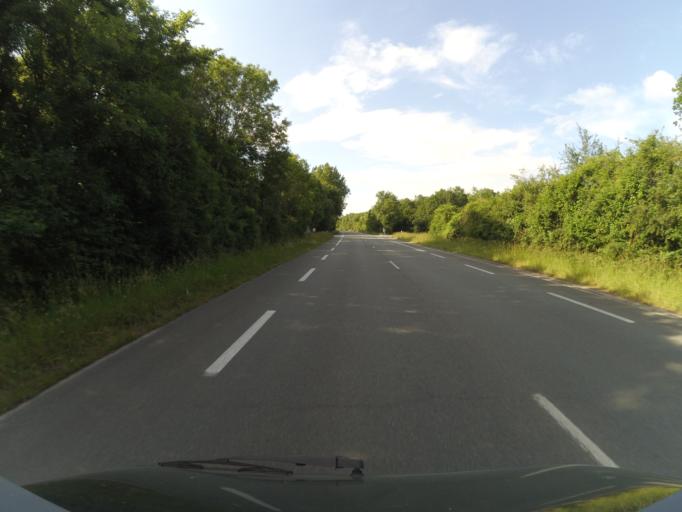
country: FR
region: Poitou-Charentes
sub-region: Departement de la Charente-Maritime
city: Saint-Agnant
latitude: 45.8206
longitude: -0.9317
